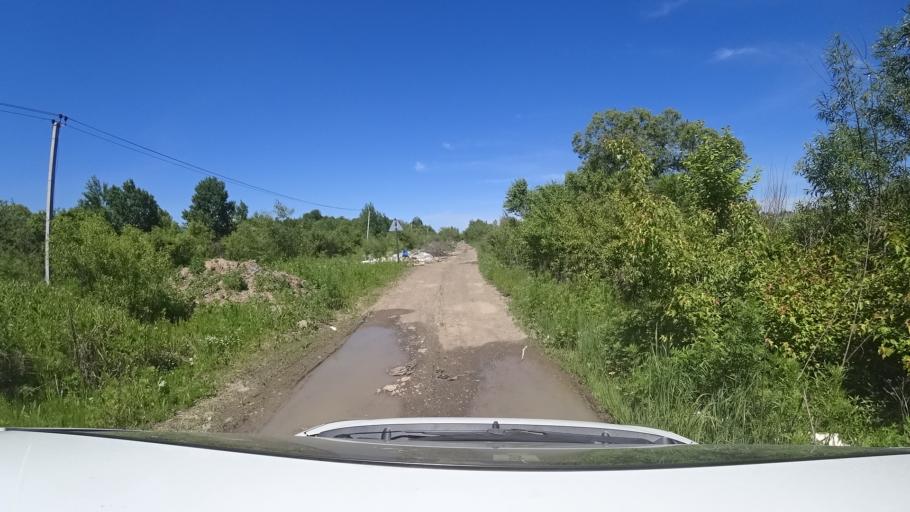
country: RU
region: Khabarovsk Krai
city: Topolevo
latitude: 48.4852
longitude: 135.1761
